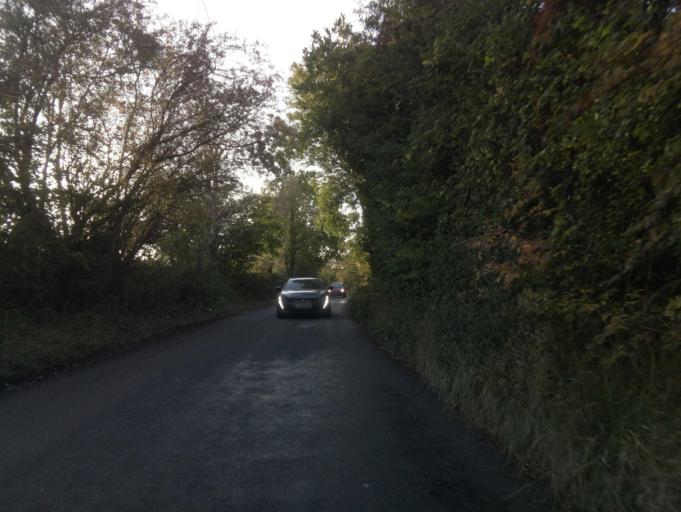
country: GB
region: England
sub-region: South Gloucestershire
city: Severn Beach
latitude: 51.5351
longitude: -2.6261
